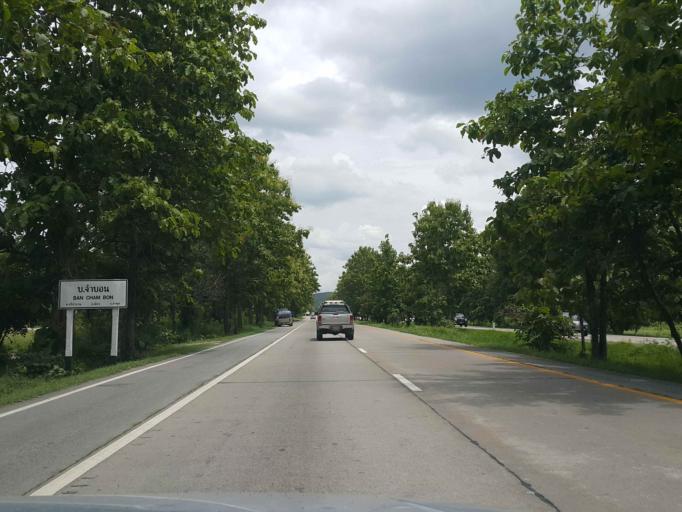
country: TH
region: Lamphun
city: Mae Tha
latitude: 18.5273
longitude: 99.0820
